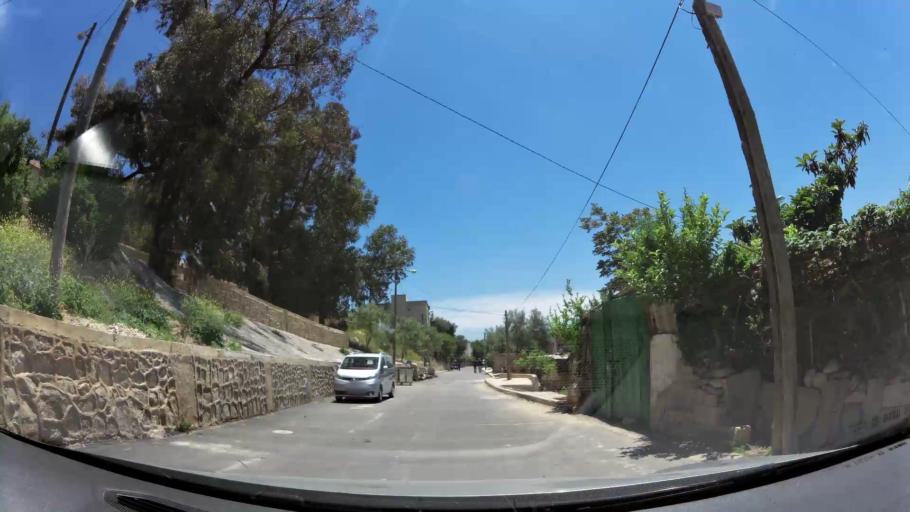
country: MA
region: Meknes-Tafilalet
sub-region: Meknes
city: Meknes
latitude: 33.9076
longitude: -5.5646
